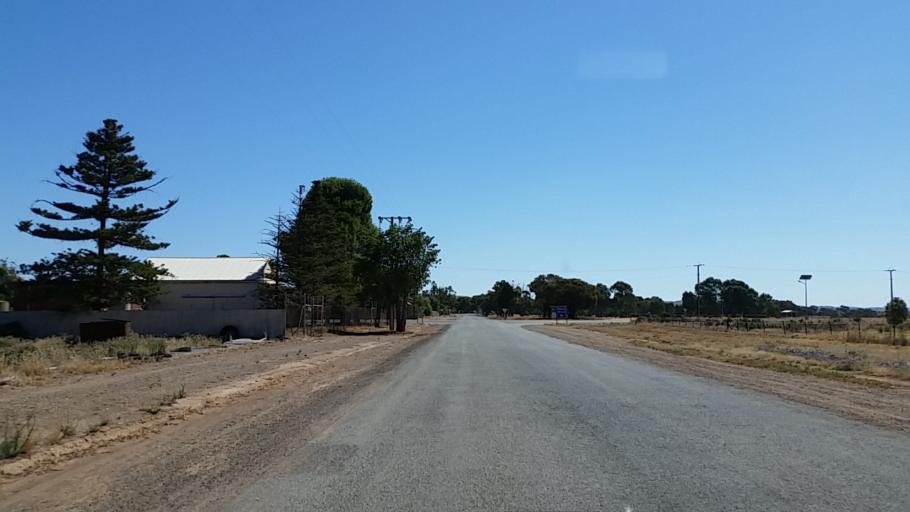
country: AU
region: South Australia
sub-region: Peterborough
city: Peterborough
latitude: -32.7312
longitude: 138.6172
